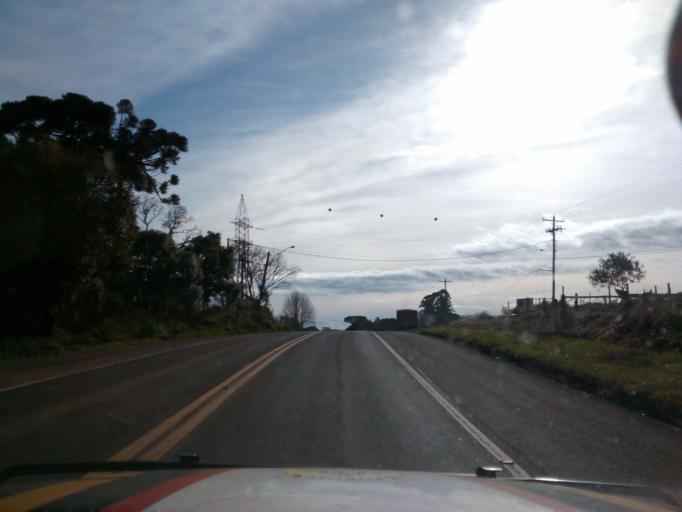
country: BR
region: Rio Grande do Sul
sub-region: Lagoa Vermelha
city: Lagoa Vermelha
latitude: -28.1868
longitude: -51.5249
